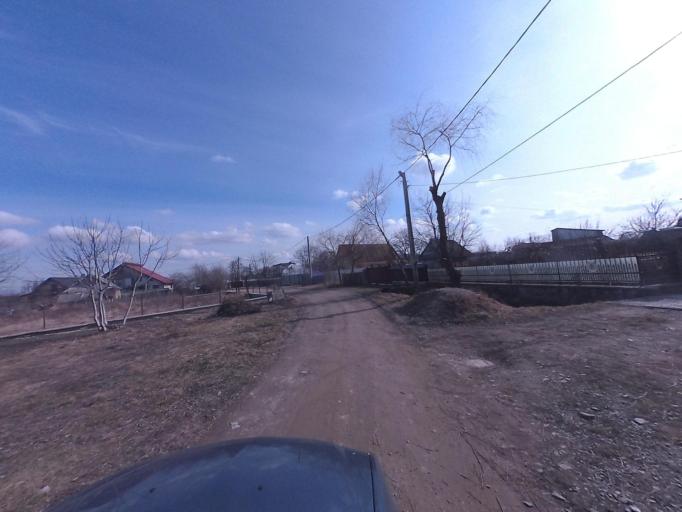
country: RO
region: Neamt
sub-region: Oras Targu Neamt
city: Targu Neamt
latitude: 47.2049
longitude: 26.3829
